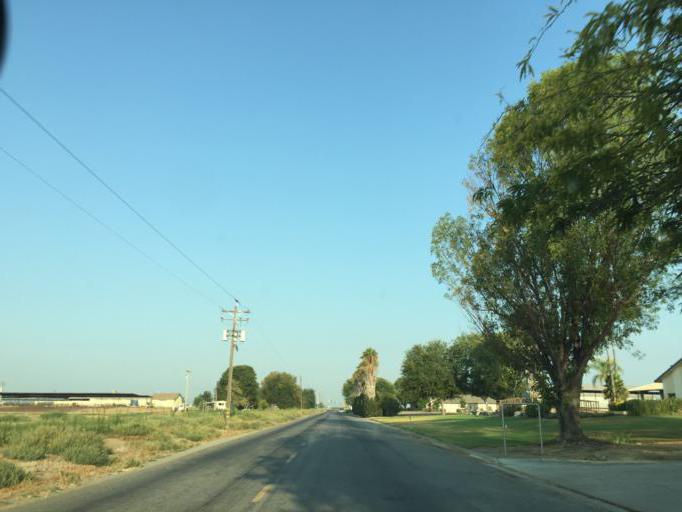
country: US
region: California
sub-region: Tulare County
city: London
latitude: 36.4439
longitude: -119.3888
